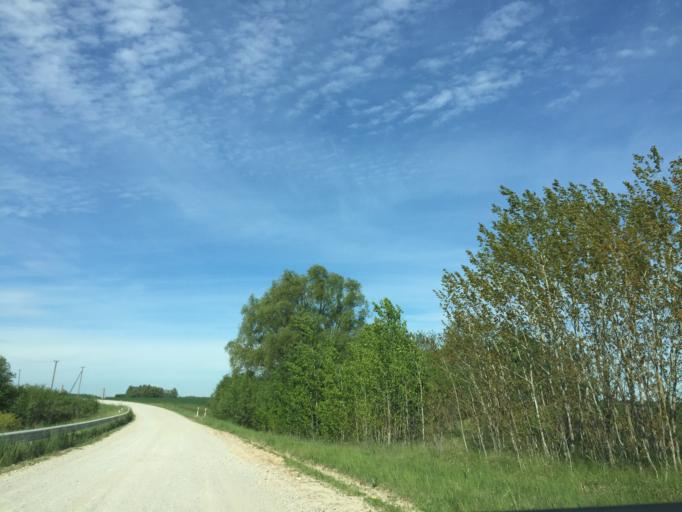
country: LT
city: Linkuva
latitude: 56.0772
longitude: 24.1097
